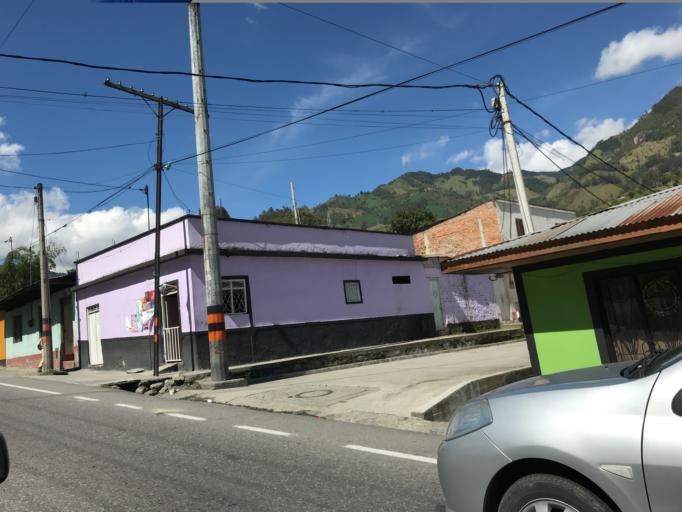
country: CO
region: Tolima
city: Cajamarca
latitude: 4.4398
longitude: -75.4320
